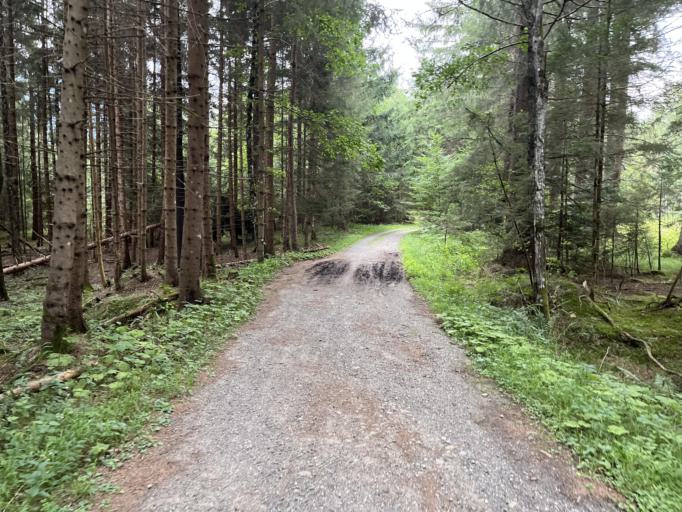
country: AT
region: Carinthia
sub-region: Politischer Bezirk Spittal an der Drau
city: Millstatt
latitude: 46.7963
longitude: 13.5441
